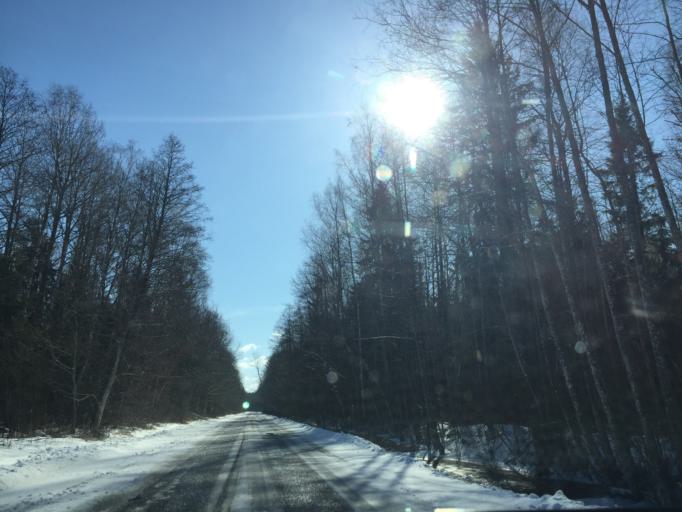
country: LV
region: Salacgrivas
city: Ainazi
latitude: 58.0004
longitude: 24.5247
